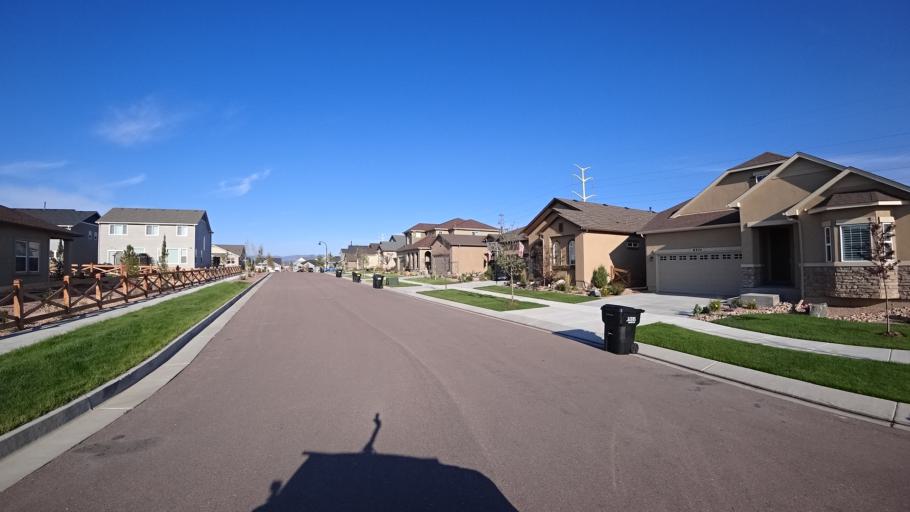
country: US
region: Colorado
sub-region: El Paso County
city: Black Forest
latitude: 38.9368
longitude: -104.6598
